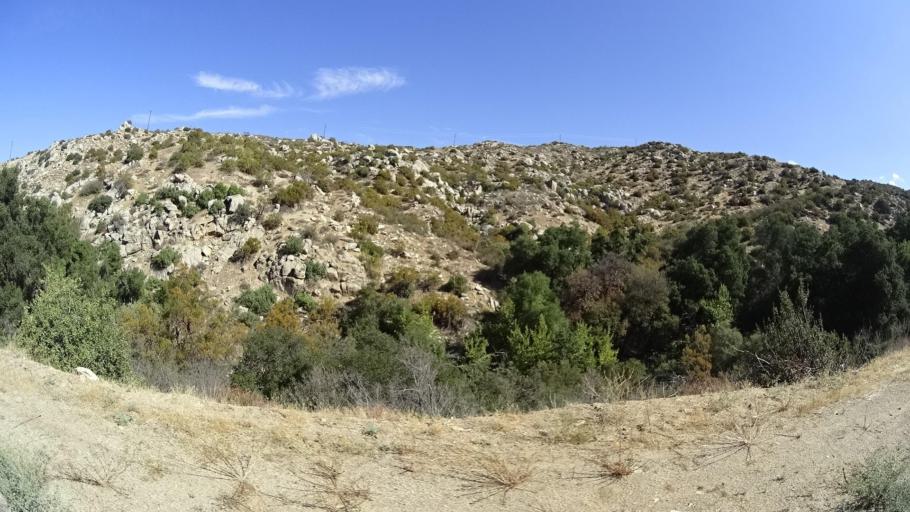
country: US
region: California
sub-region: Riverside County
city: Aguanga
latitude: 33.3744
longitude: -116.7180
